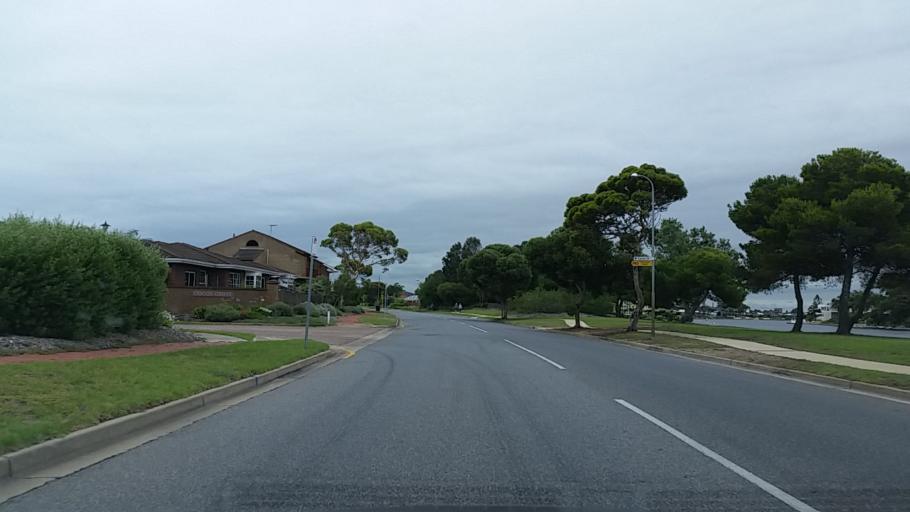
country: AU
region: South Australia
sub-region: Charles Sturt
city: West Lakes Shore
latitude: -34.8720
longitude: 138.4923
